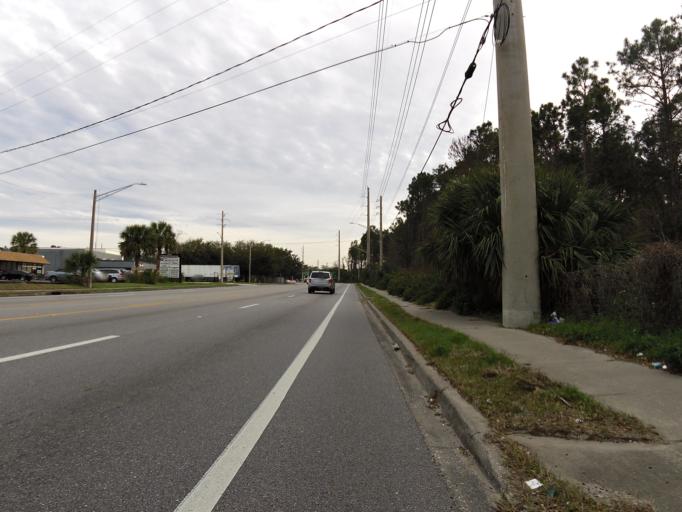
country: US
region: Florida
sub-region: Duval County
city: Jacksonville
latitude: 30.2558
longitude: -81.6173
